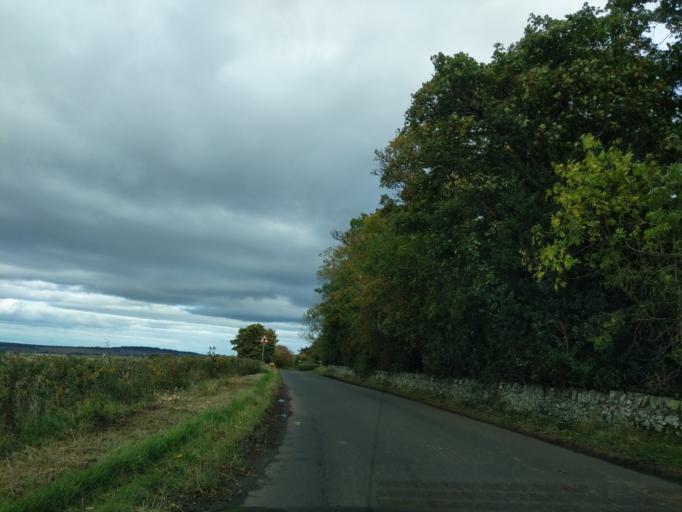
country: GB
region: Scotland
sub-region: East Lothian
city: Haddington
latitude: 55.9363
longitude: -2.7186
